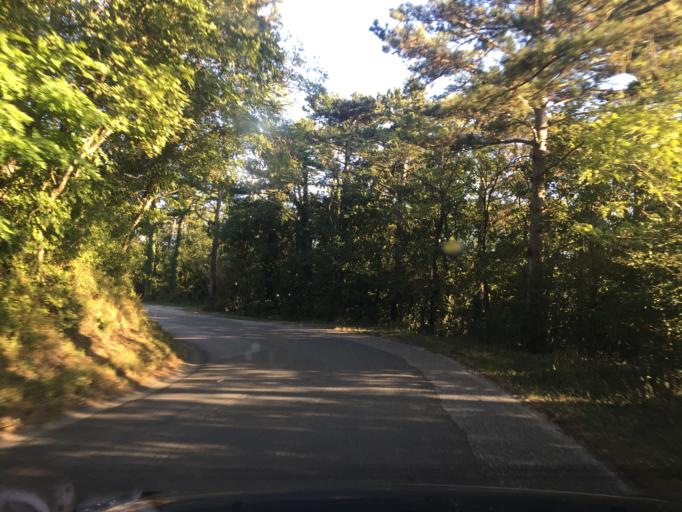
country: SI
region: Vipava
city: Vipava
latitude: 45.7929
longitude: 13.9847
